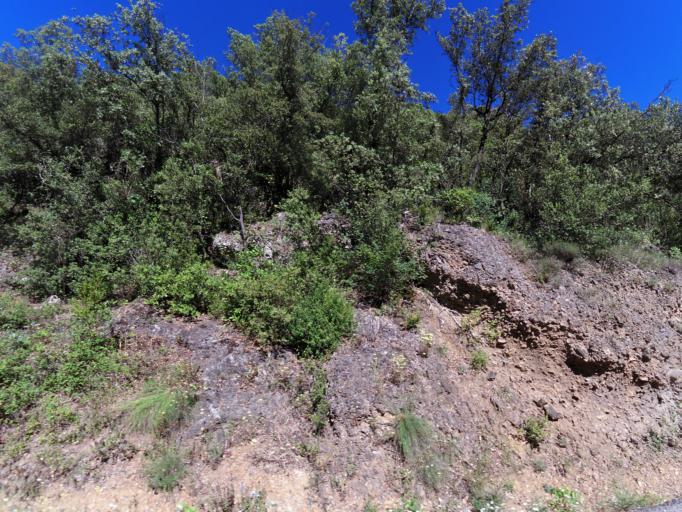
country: FR
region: Languedoc-Roussillon
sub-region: Departement du Gard
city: Saint-Jean-du-Gard
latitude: 44.0951
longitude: 3.9189
